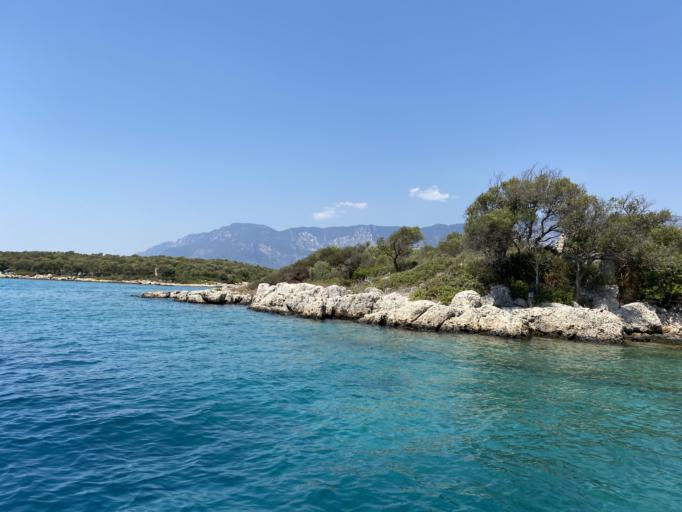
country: TR
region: Mugla
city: Yerkesik
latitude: 36.9966
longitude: 28.2110
